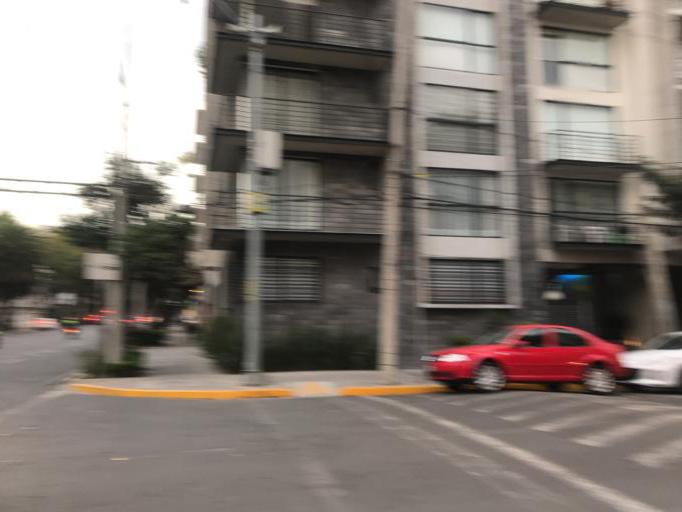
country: MX
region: Mexico City
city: Colonia del Valle
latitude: 19.3807
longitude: -99.1565
